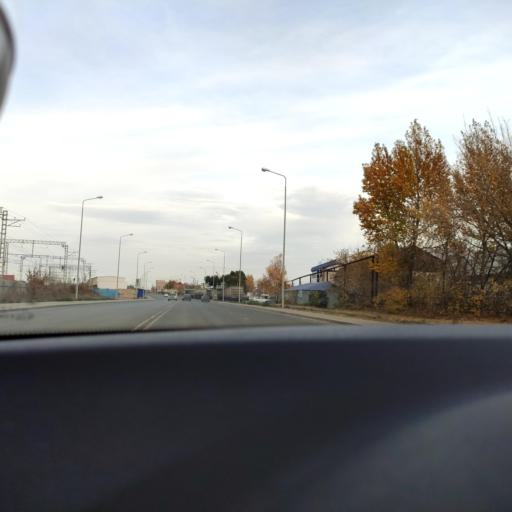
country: RU
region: Samara
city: Samara
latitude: 53.1789
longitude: 50.2055
